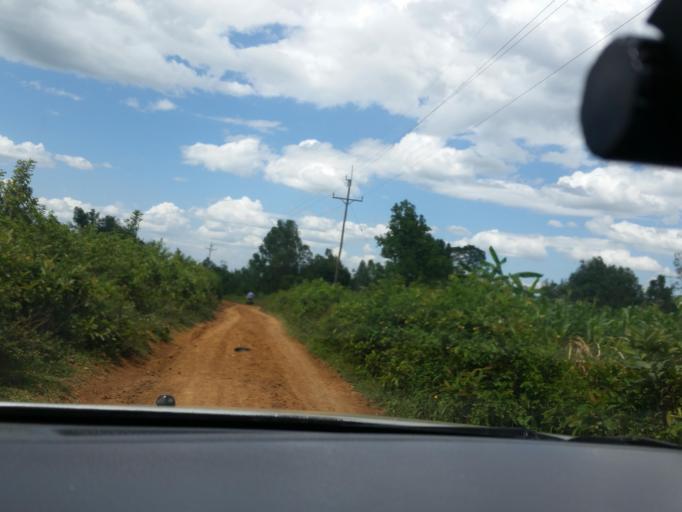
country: KE
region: Siaya
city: Yala
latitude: 0.0977
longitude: 34.4130
